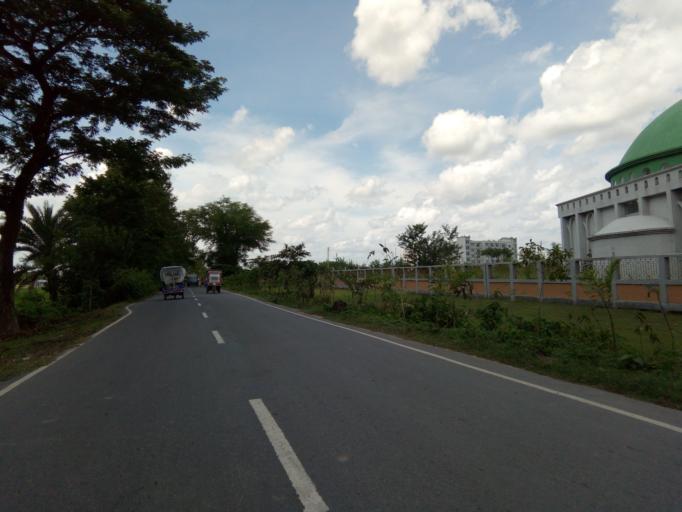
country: BD
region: Dhaka
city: Tungipara
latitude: 22.9630
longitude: 89.8168
